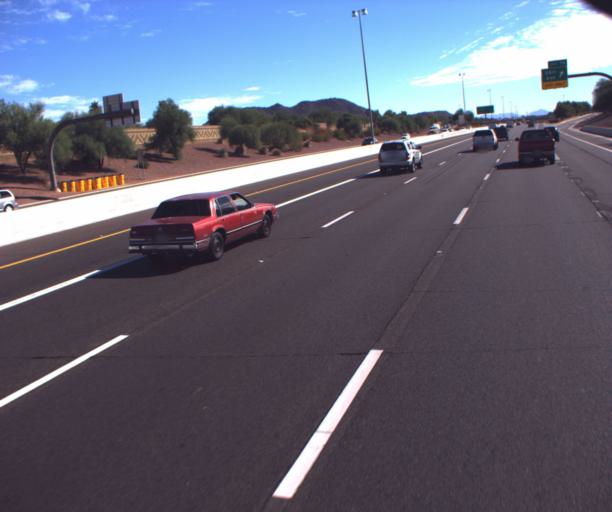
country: US
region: Arizona
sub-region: Maricopa County
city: Peoria
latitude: 33.6681
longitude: -112.1941
